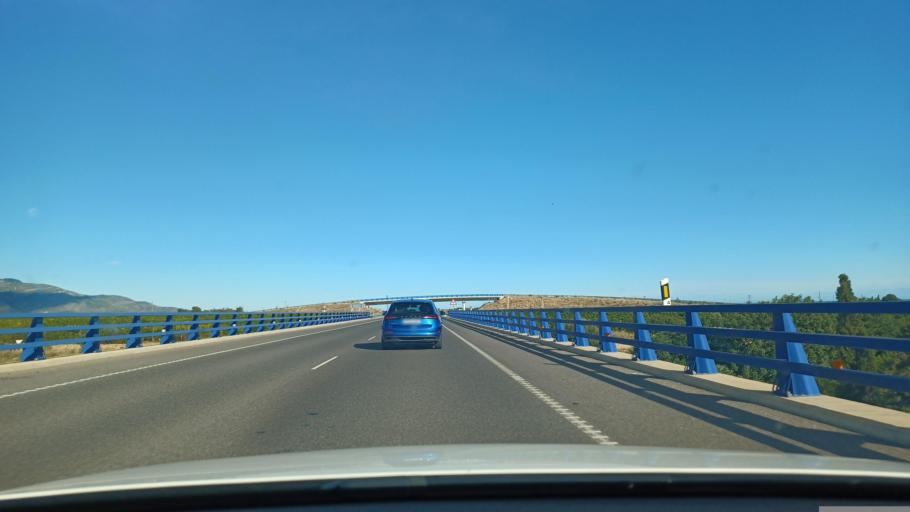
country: ES
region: Valencia
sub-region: Provincia de Castello
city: Vinaros
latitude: 40.5040
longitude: 0.4732
